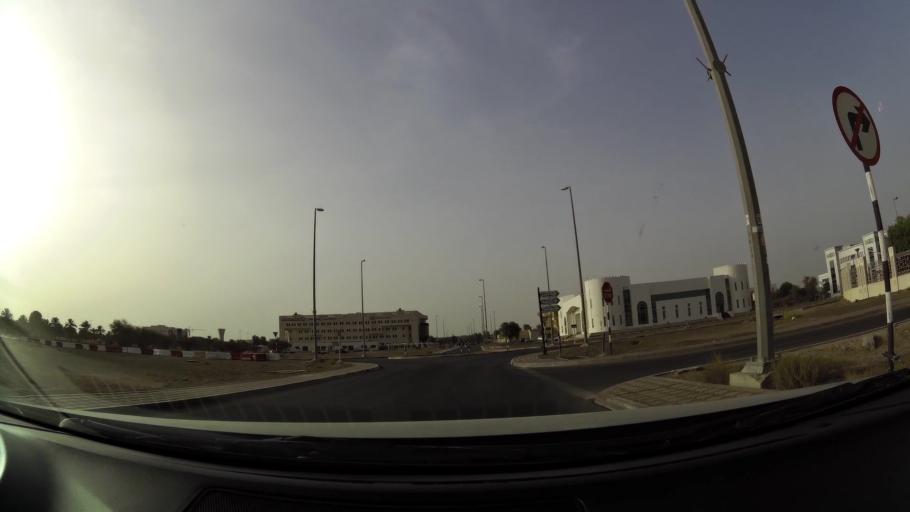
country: AE
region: Abu Dhabi
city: Al Ain
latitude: 24.2380
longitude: 55.7304
